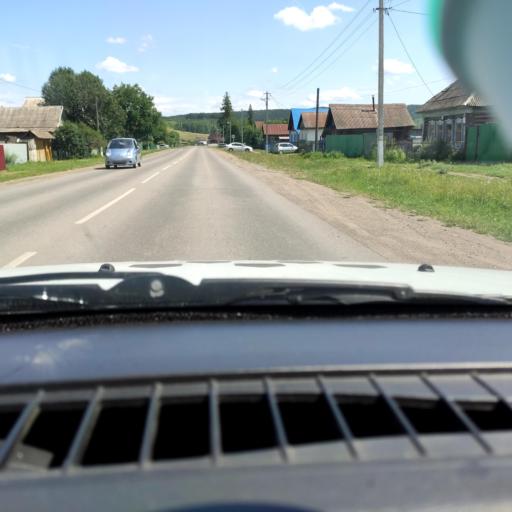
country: RU
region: Bashkortostan
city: Mesyagutovo
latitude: 55.5297
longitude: 58.2702
